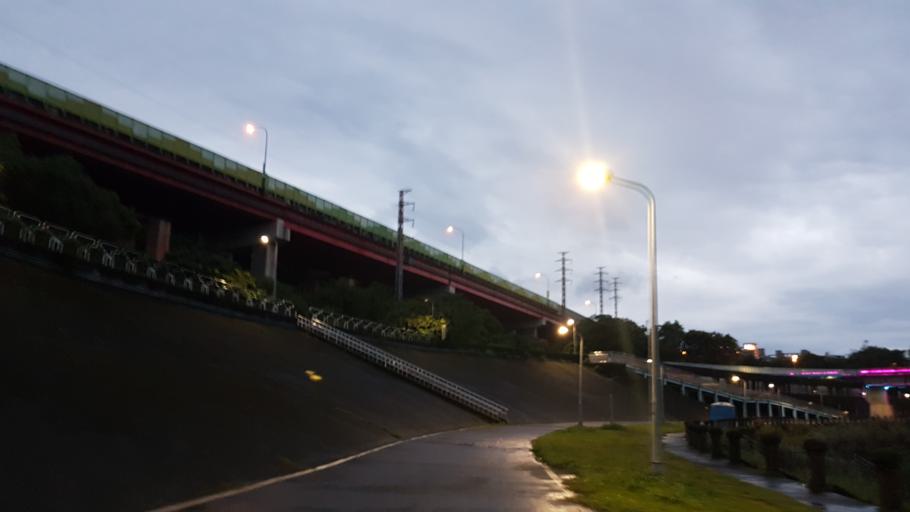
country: TW
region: Taipei
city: Taipei
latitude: 24.9768
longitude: 121.5576
